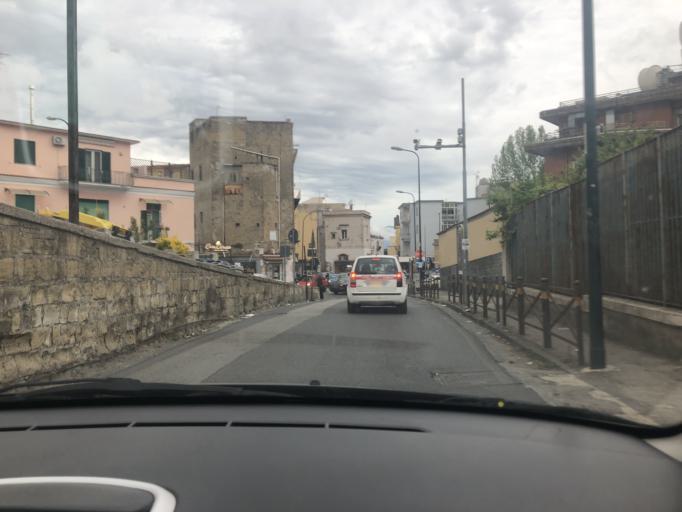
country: IT
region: Campania
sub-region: Provincia di Napoli
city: Napoli
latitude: 40.8641
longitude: 14.2184
